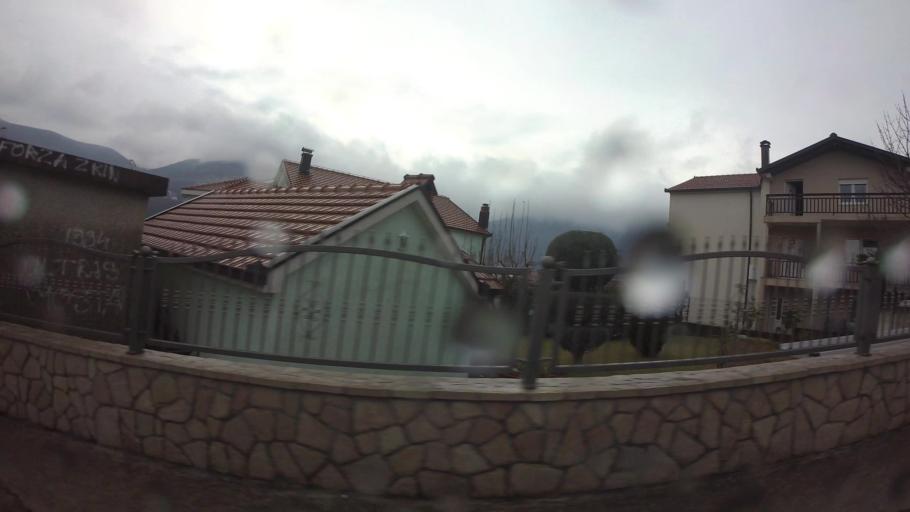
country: BA
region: Federation of Bosnia and Herzegovina
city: Cim
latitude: 43.3488
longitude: 17.7769
